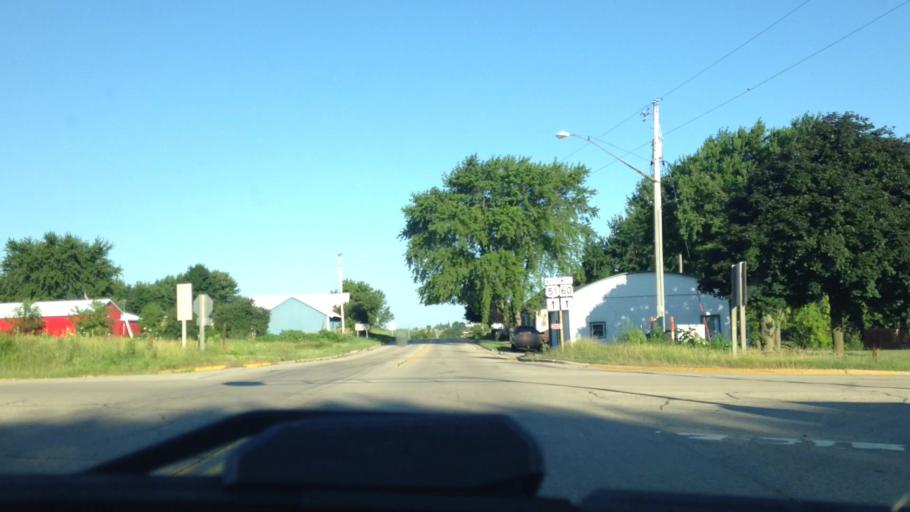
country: US
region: Wisconsin
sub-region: Dane County
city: De Forest
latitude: 43.3322
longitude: -89.3251
